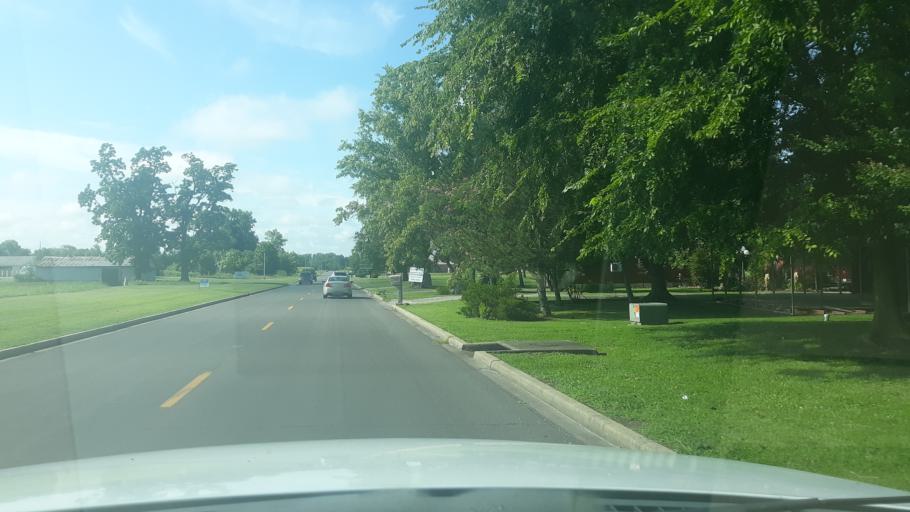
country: US
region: Illinois
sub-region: Williamson County
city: Energy
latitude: 37.7395
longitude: -88.9933
